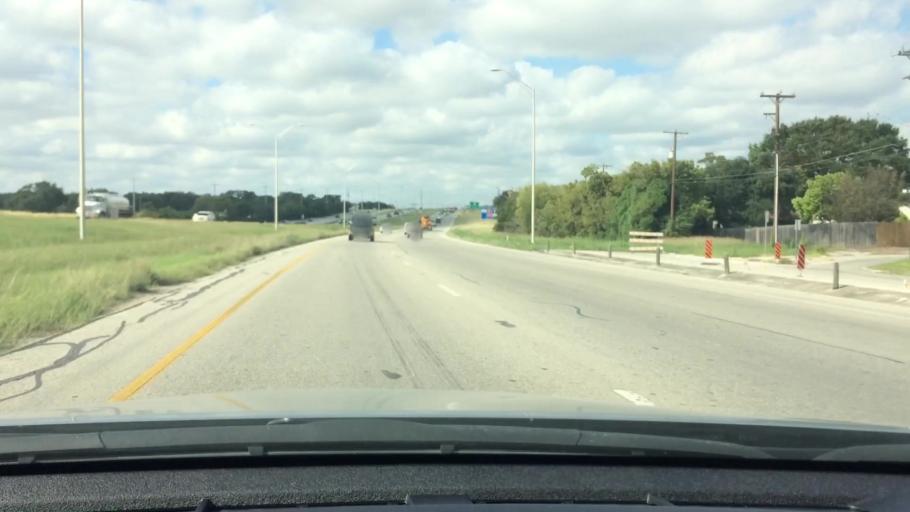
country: US
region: Texas
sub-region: Bexar County
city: Live Oak
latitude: 29.5498
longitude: -98.3189
